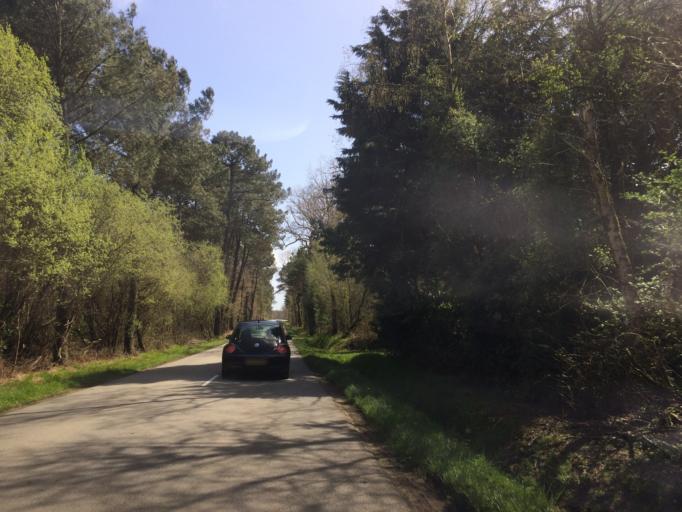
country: FR
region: Brittany
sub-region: Departement du Morbihan
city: La Trinite-sur-Mer
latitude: 47.6109
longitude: -3.0492
